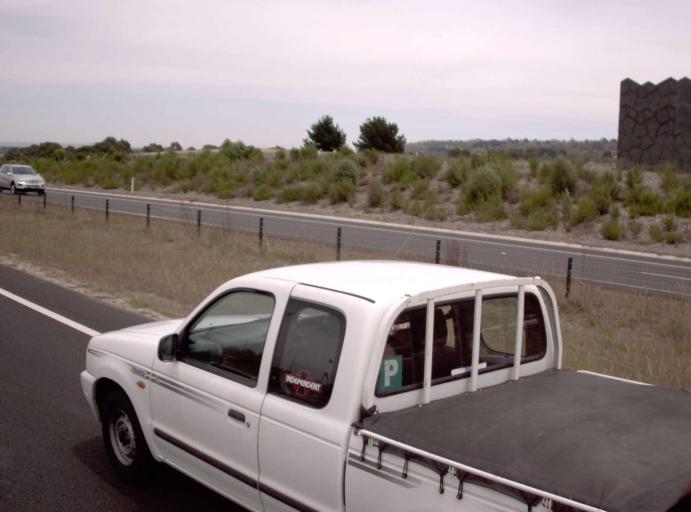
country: AU
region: Victoria
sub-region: Mornington Peninsula
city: Baxter
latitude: -38.1861
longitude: 145.1573
